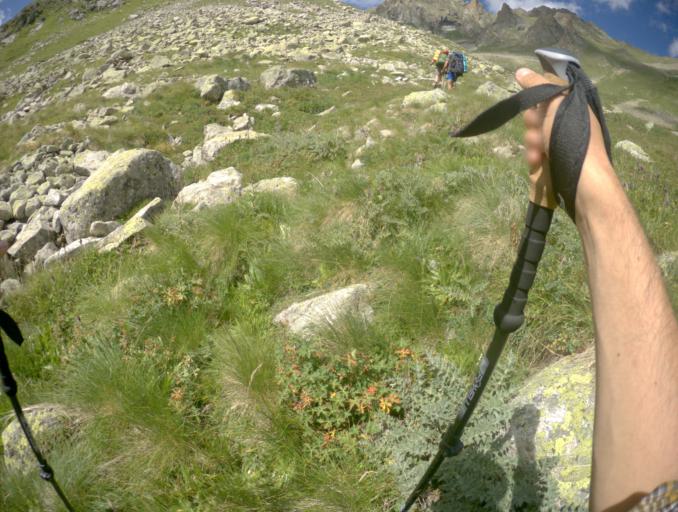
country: RU
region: Karachayevo-Cherkesiya
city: Uchkulan
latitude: 43.3264
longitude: 42.0967
